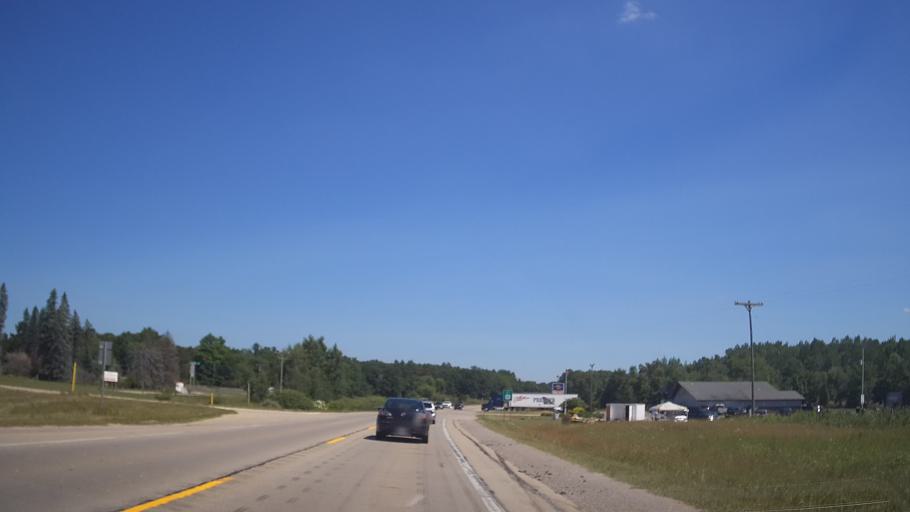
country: US
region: Michigan
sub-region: Clare County
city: Clare
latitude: 43.8686
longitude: -84.9174
